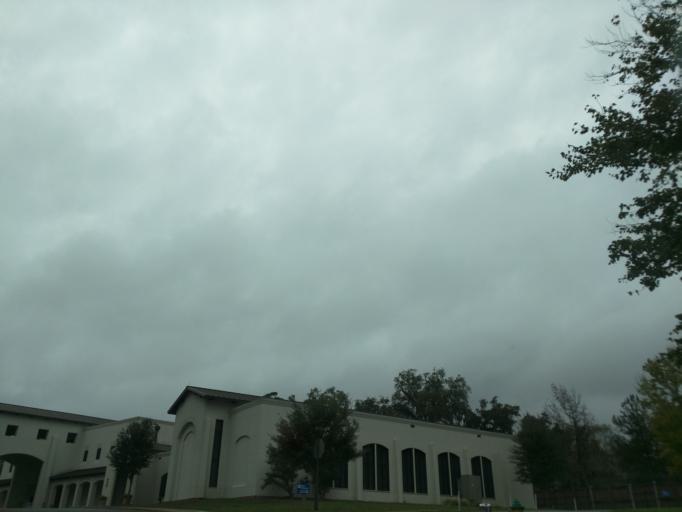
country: US
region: Florida
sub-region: Leon County
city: Tallahassee
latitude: 30.4483
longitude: -84.3194
